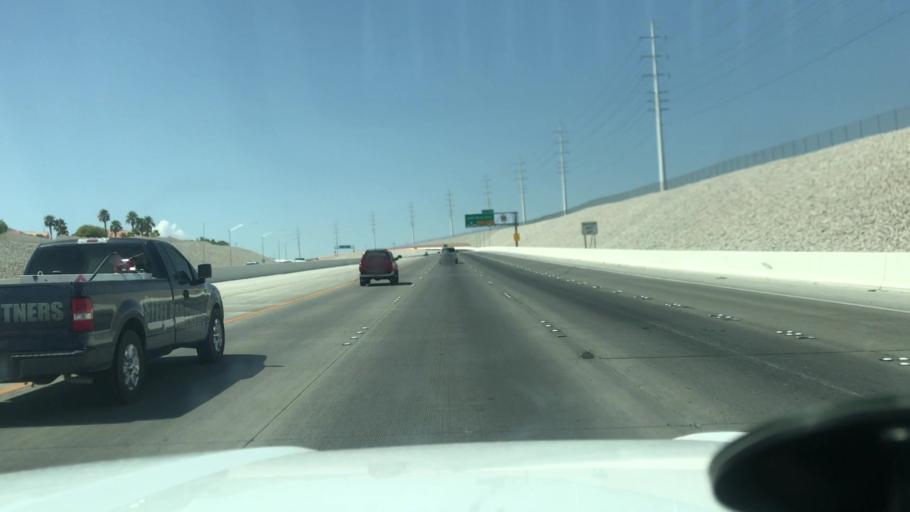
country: US
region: Nevada
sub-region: Clark County
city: Summerlin South
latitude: 36.2124
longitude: -115.3352
